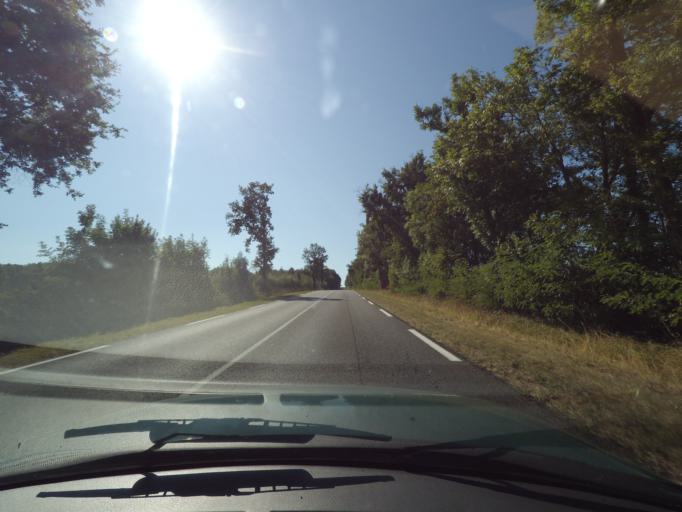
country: FR
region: Poitou-Charentes
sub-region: Departement de la Vienne
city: Lussac-les-Chateaux
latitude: 46.3582
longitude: 0.7786
